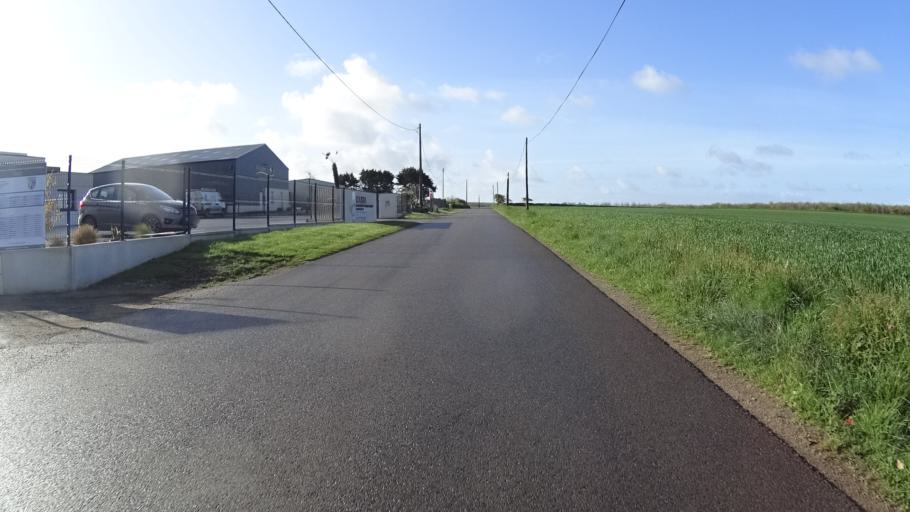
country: FR
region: Brittany
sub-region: Departement du Finistere
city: Plouarzel
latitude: 48.4320
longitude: -4.7153
